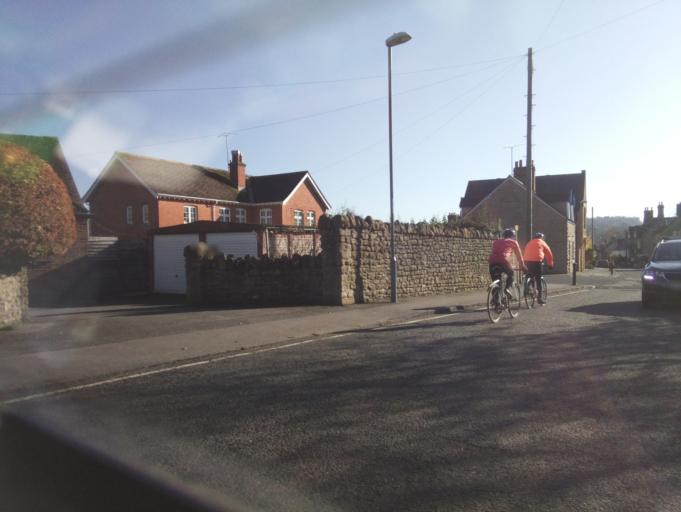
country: GB
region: England
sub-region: Dorset
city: Sherborne
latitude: 50.9491
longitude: -2.5215
